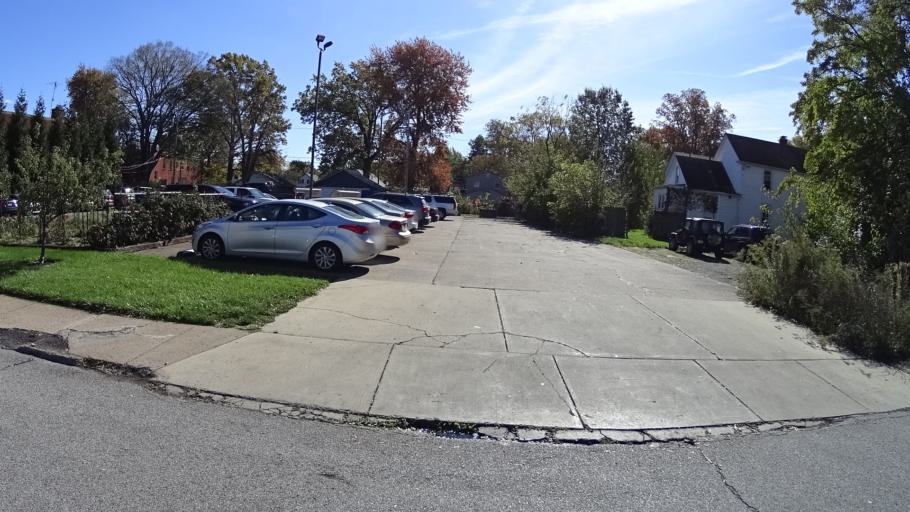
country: US
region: Ohio
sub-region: Lorain County
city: Lorain
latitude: 41.4636
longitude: -82.1774
